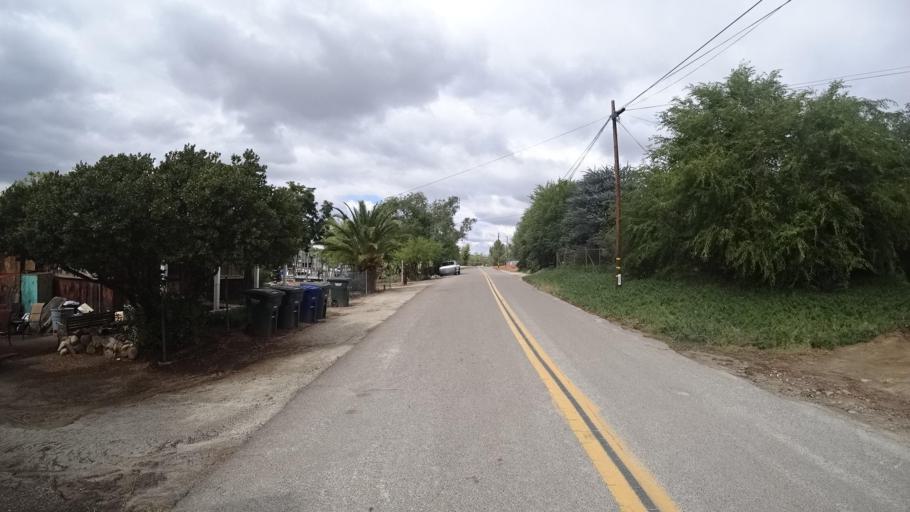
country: US
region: California
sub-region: San Diego County
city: Campo
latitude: 32.6273
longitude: -116.4710
